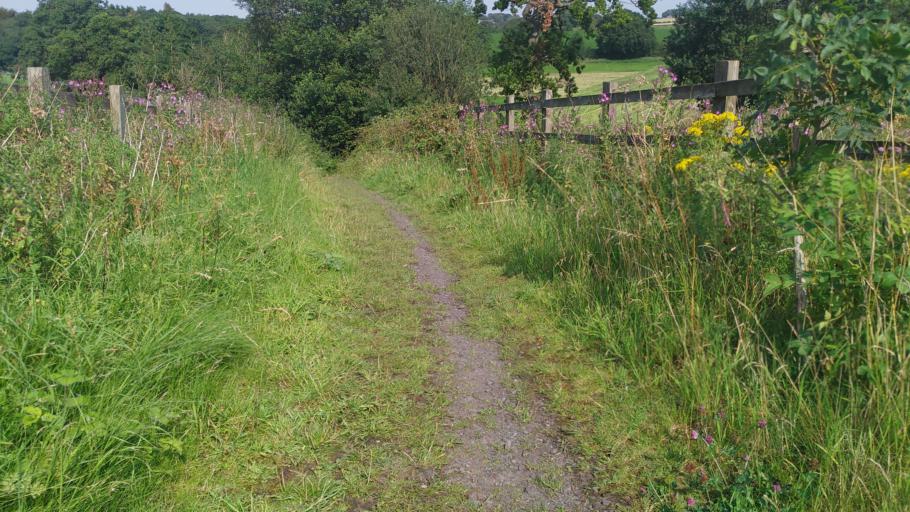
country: GB
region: England
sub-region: Lancashire
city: Clayton-le-Woods
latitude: 53.7187
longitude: -2.6238
